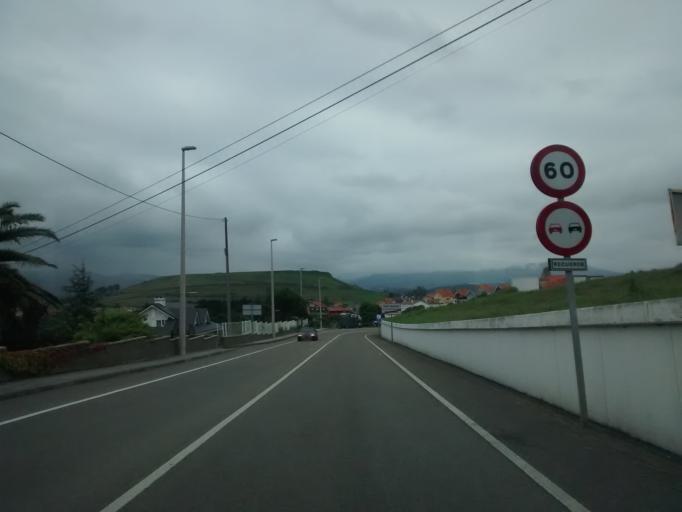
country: ES
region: Cantabria
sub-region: Provincia de Cantabria
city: Suances
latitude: 43.4167
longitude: -4.0385
